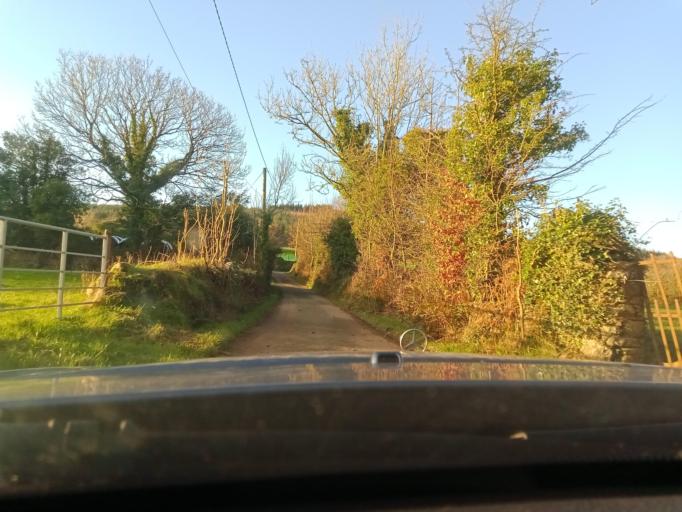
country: IE
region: Leinster
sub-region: Kilkenny
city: Graiguenamanagh
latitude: 52.4885
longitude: -6.9492
